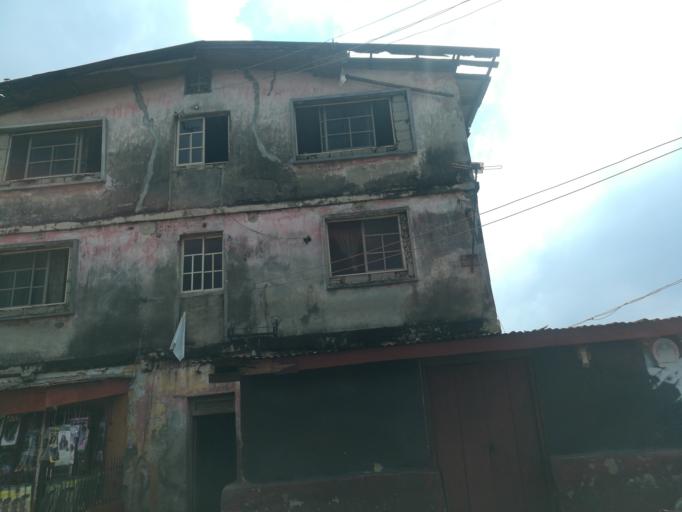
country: NG
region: Lagos
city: Mushin
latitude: 6.5280
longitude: 3.3656
